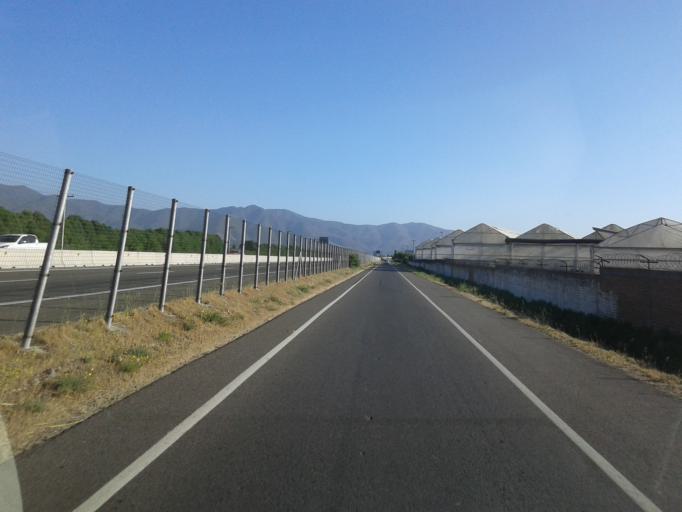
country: CL
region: Valparaiso
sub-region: Provincia de Quillota
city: Quillota
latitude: -32.8504
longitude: -71.2245
